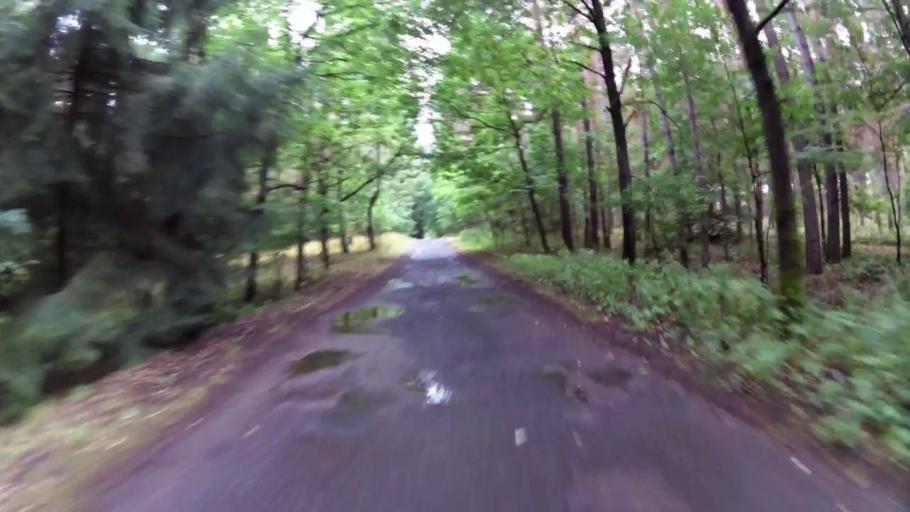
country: PL
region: West Pomeranian Voivodeship
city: Trzcinsko Zdroj
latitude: 52.8926
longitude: 14.7031
